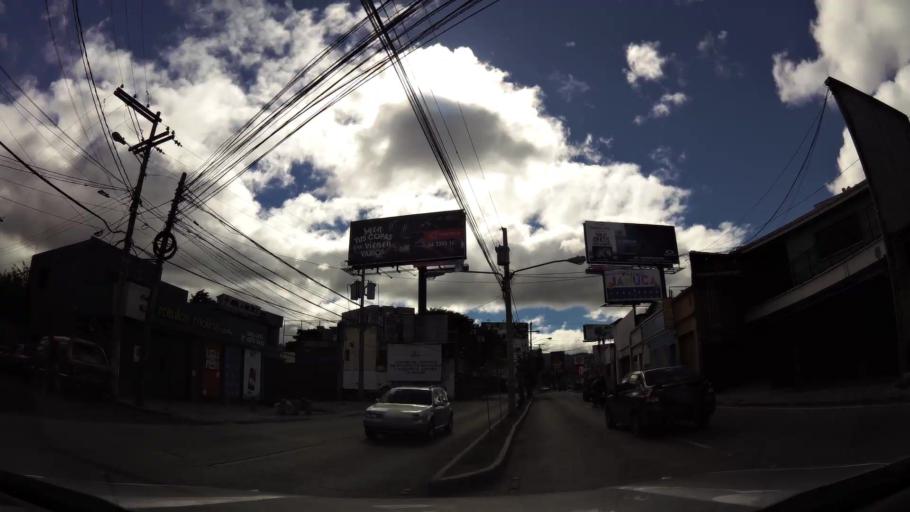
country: GT
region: Guatemala
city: Santa Catarina Pinula
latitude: 14.5901
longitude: -90.5035
